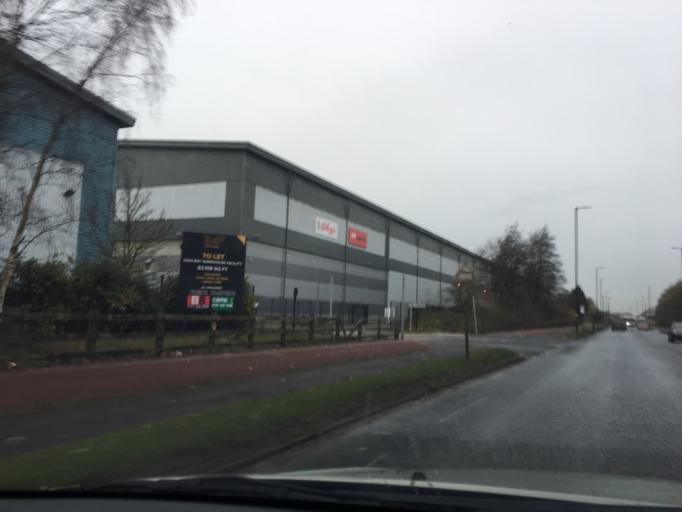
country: GB
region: England
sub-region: Trafford
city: Stretford
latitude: 53.4582
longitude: -2.3227
